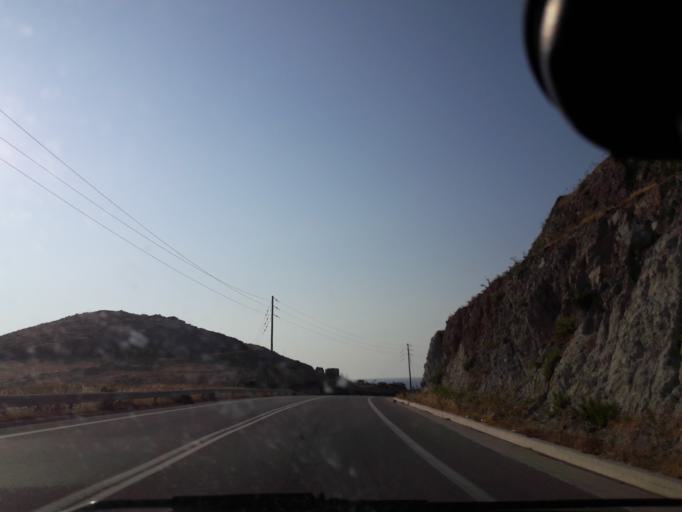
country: GR
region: North Aegean
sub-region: Nomos Lesvou
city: Myrina
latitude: 39.8619
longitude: 25.0564
